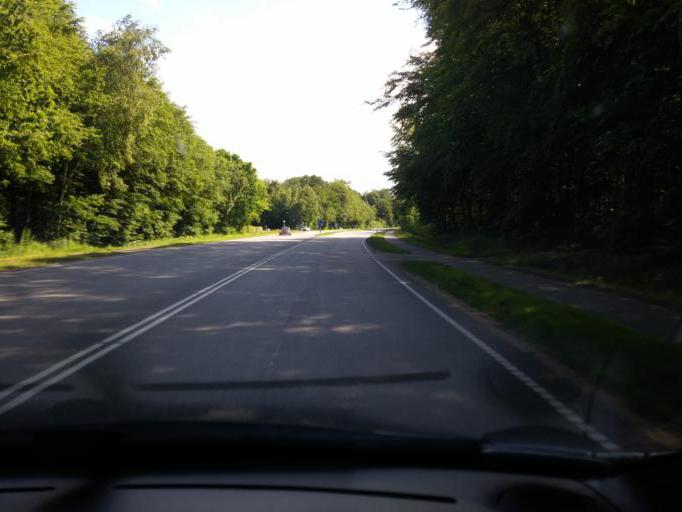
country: DK
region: Capital Region
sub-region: Hillerod Kommune
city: Nodebo
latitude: 55.9567
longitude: 12.3328
